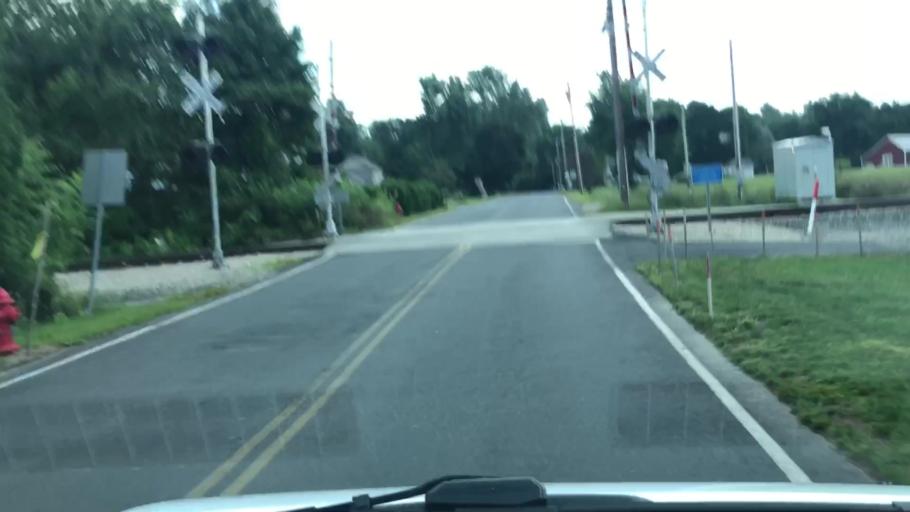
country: US
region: Massachusetts
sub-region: Hampshire County
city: Hatfield
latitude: 42.3815
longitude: -72.6296
